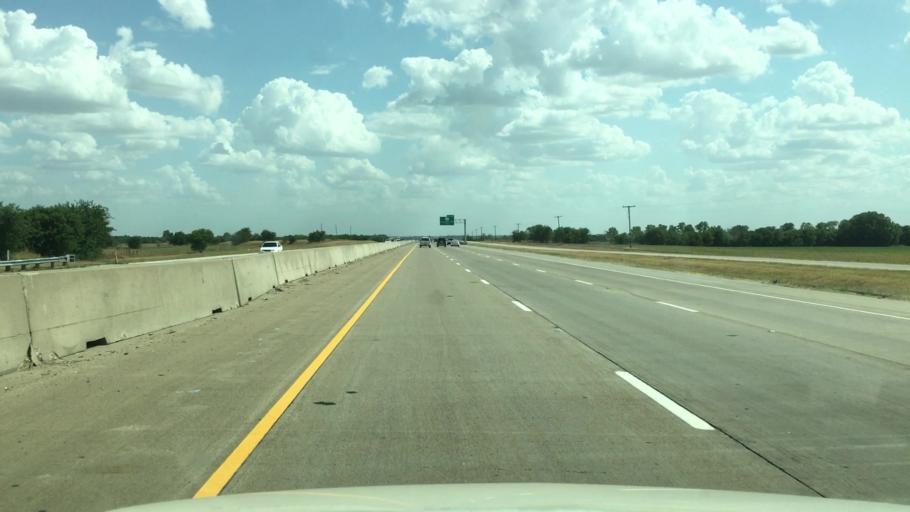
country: US
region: Texas
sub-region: Ellis County
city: Nash
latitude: 32.2790
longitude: -96.8690
